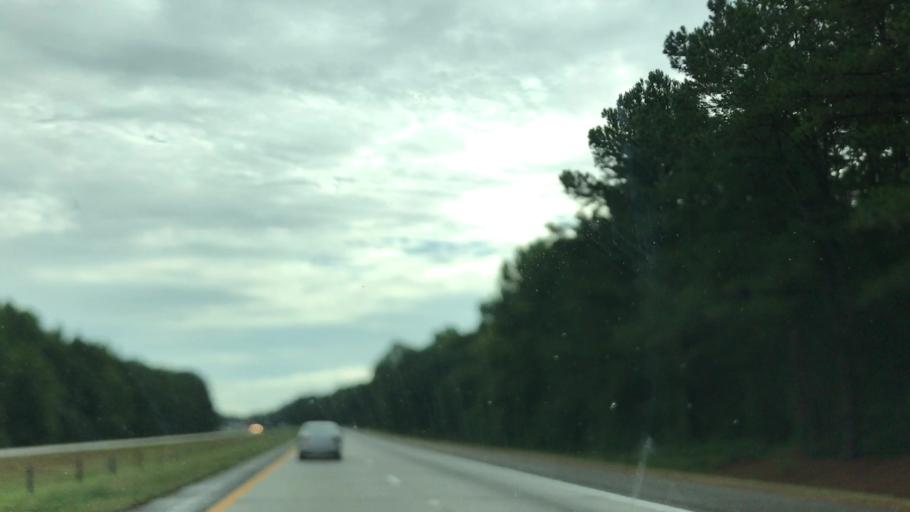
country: US
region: North Carolina
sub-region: Nash County
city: Nashville
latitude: 35.9261
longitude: -77.9082
